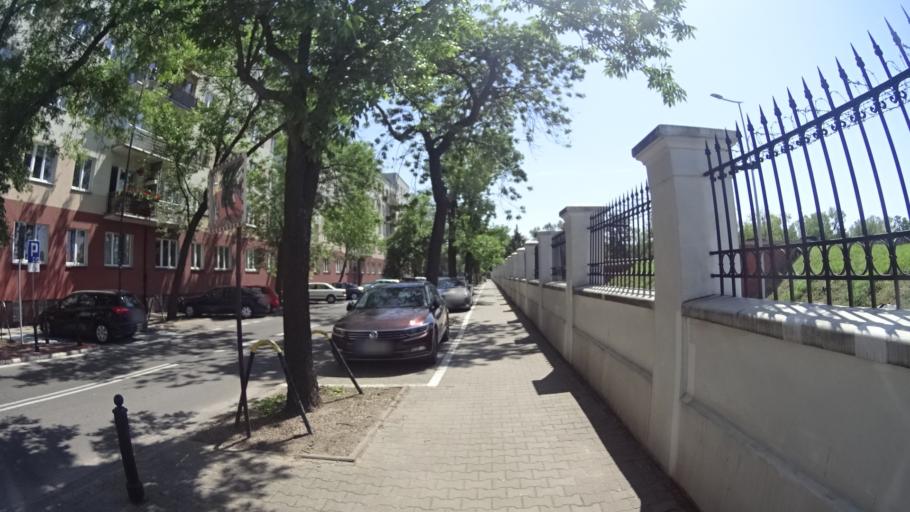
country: PL
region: Masovian Voivodeship
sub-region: Warszawa
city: Ochota
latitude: 52.2208
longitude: 20.9998
